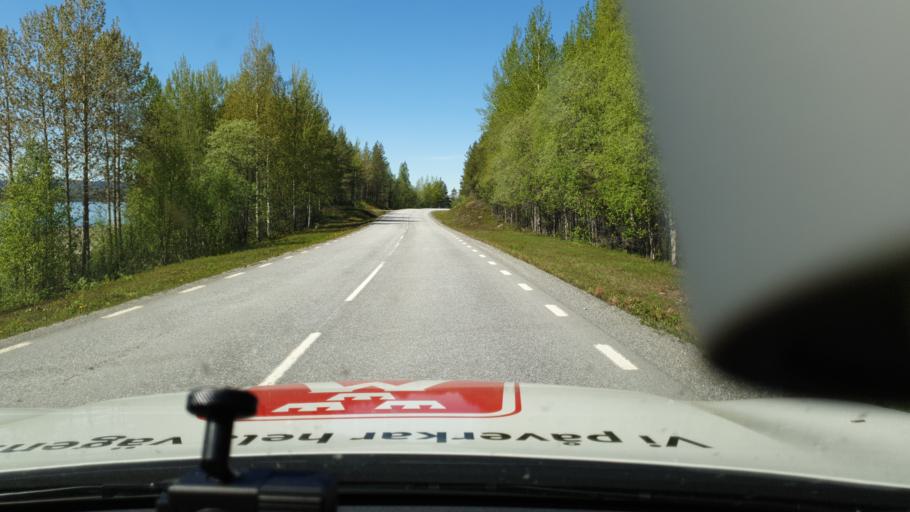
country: SE
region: Vaesterbotten
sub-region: Storumans Kommun
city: Storuman
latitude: 65.1596
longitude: 17.0526
